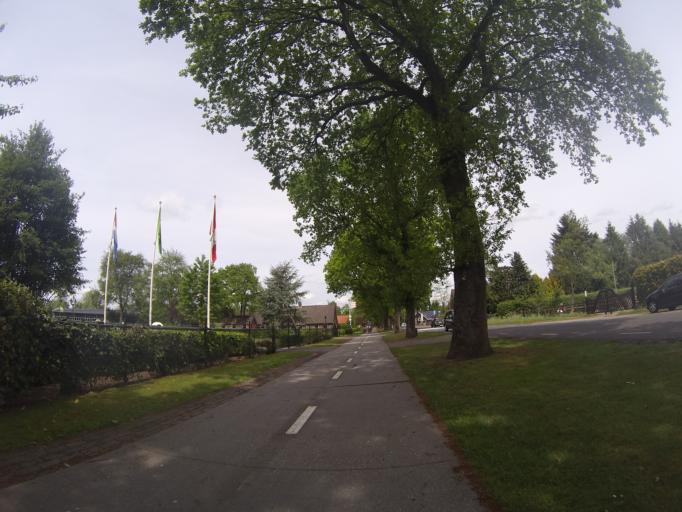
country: NL
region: Drenthe
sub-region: Gemeente Borger-Odoorn
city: Borger
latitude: 52.8560
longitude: 6.7505
